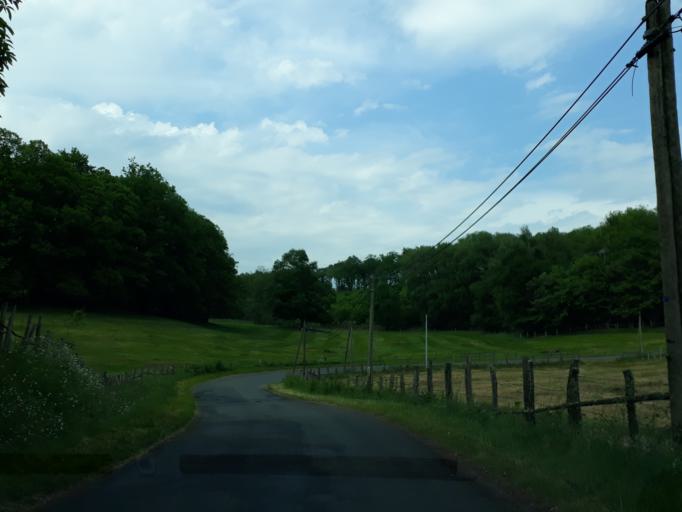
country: FR
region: Limousin
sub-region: Departement de la Correze
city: Beynat
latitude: 45.1172
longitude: 1.7510
